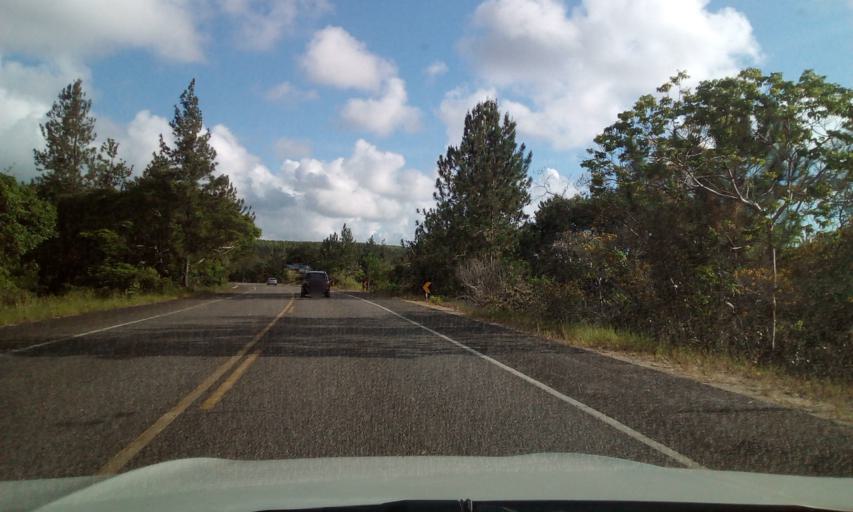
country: BR
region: Bahia
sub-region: Entre Rios
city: Entre Rios
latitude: -12.1421
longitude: -37.7922
